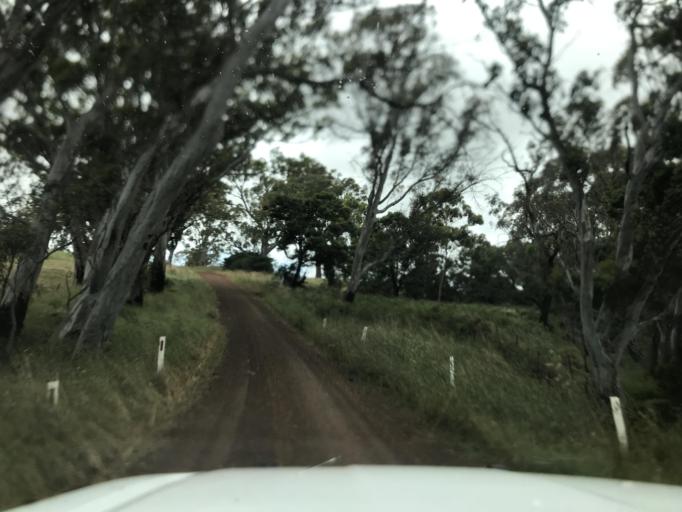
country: AU
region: South Australia
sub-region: Wattle Range
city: Penola
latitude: -37.2355
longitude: 141.4704
